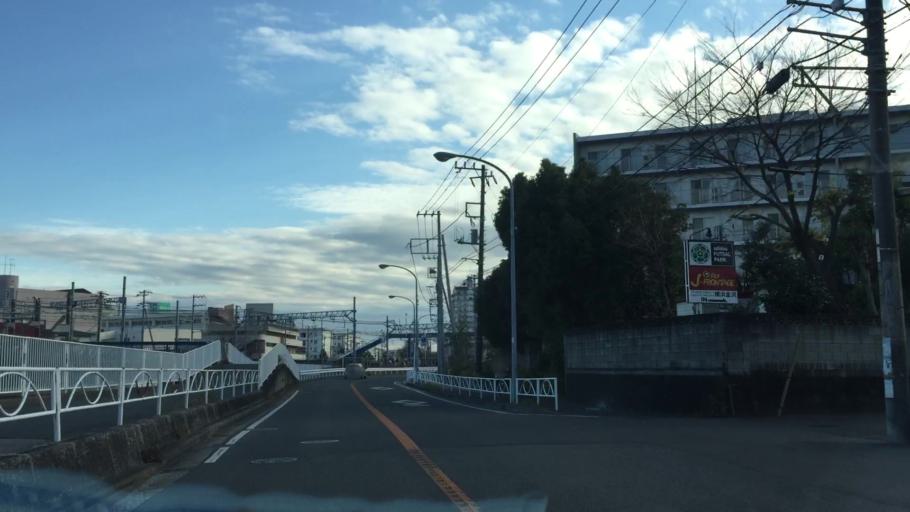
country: JP
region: Kanagawa
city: Zushi
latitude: 35.3404
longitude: 139.6199
